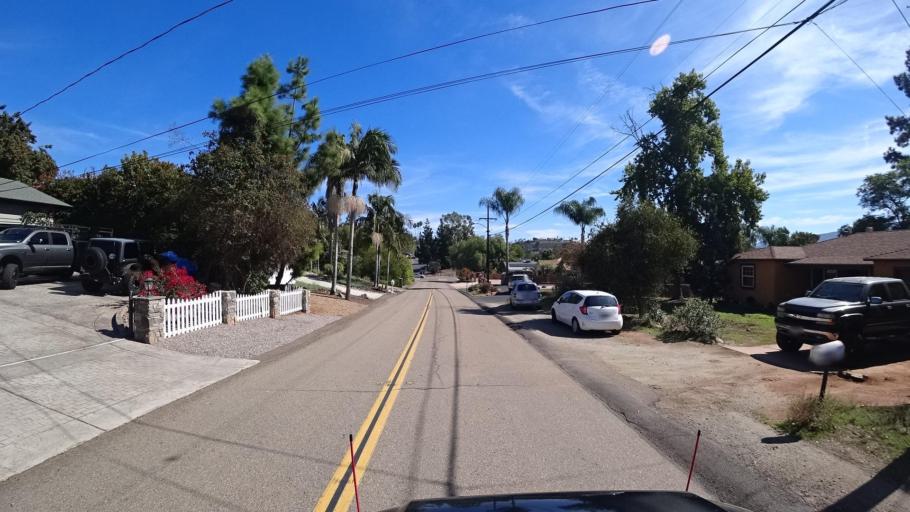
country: US
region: California
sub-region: San Diego County
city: Casa de Oro-Mount Helix
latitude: 32.7519
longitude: -116.9632
